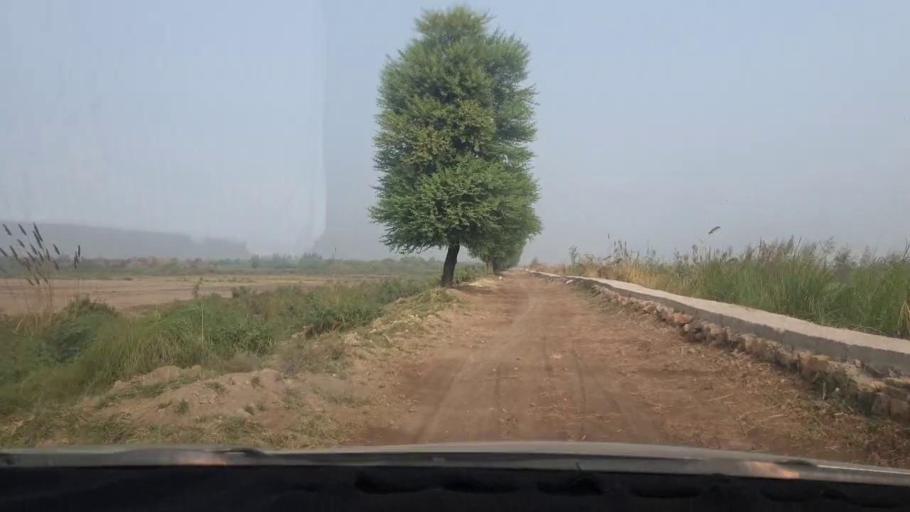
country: PK
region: Sindh
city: Matiari
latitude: 25.6637
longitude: 68.5596
